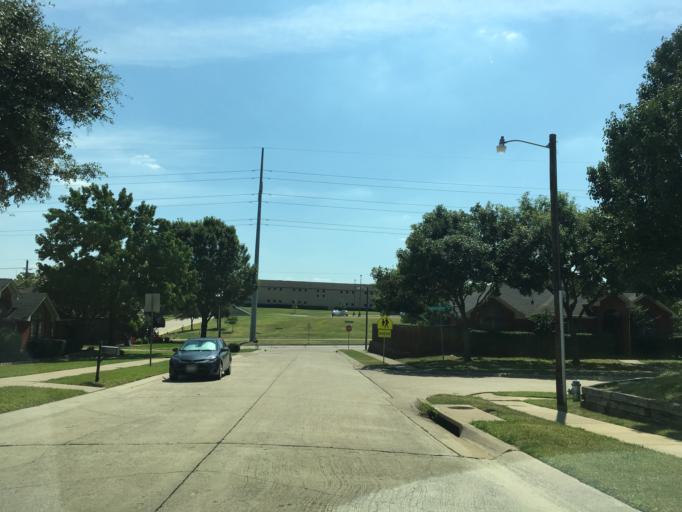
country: US
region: Texas
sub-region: Denton County
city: Lewisville
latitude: 33.0124
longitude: -97.0058
